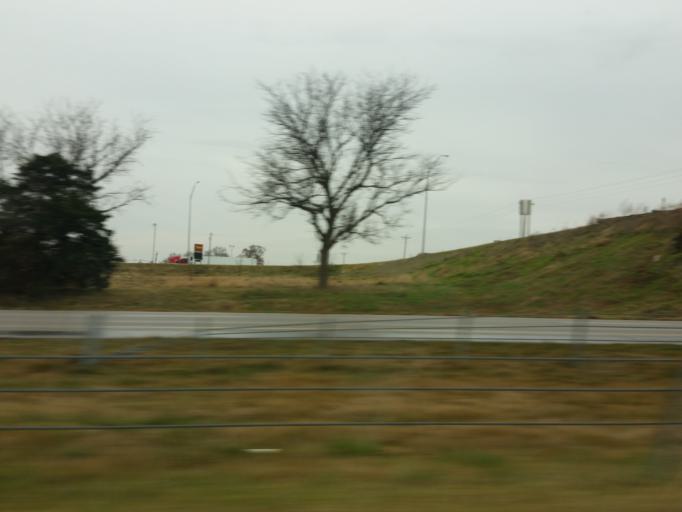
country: US
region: Iowa
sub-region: Cedar County
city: Tipton
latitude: 41.6462
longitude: -91.1513
